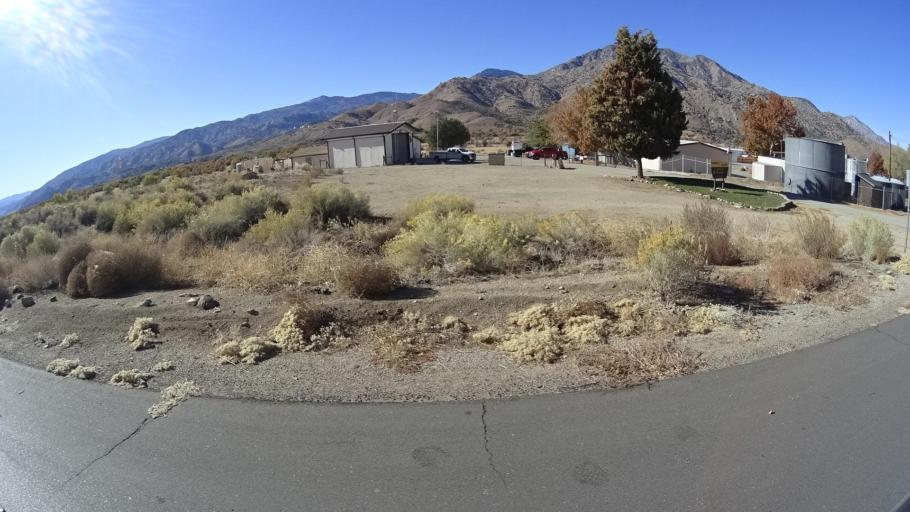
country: US
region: California
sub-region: Kern County
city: Kernville
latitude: 35.7206
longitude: -118.4166
